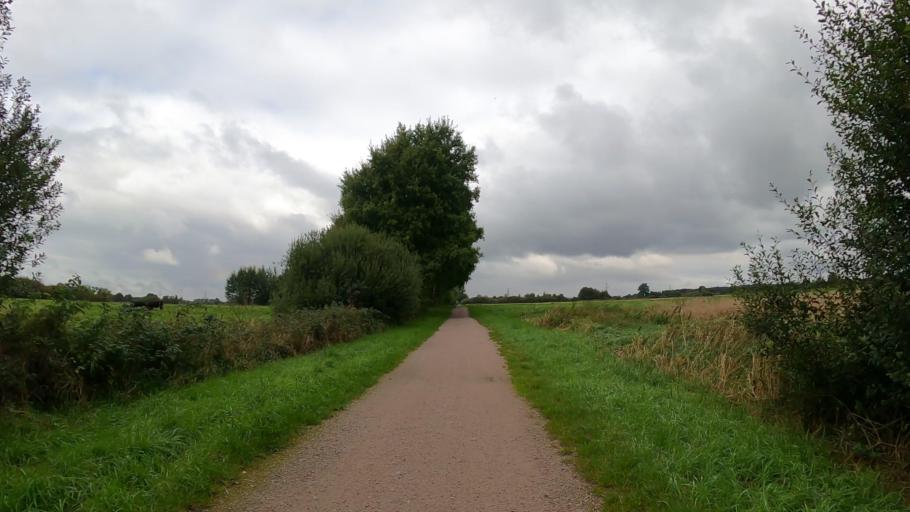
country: DE
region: Lower Saxony
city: Neu Wulmstorf
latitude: 53.4743
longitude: 9.7735
